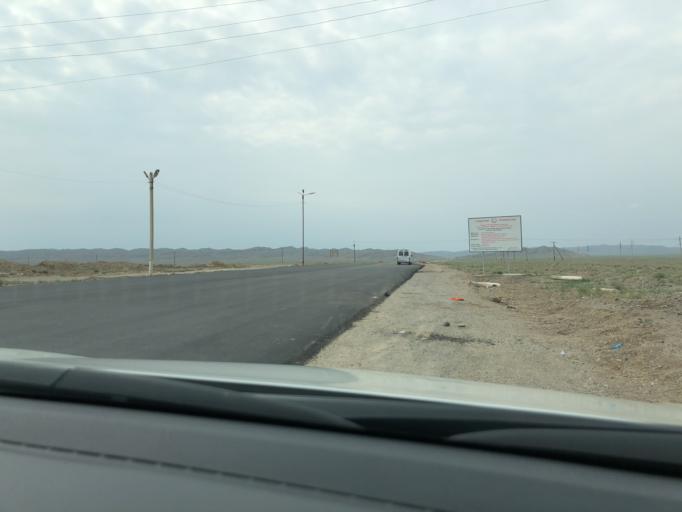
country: TJ
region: Viloyati Sughd
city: Kim
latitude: 40.1994
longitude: 70.4828
